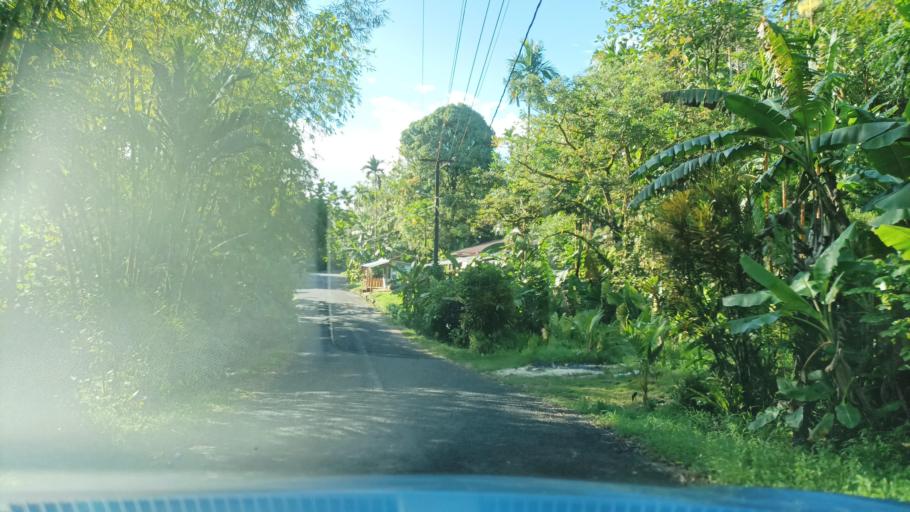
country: FM
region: Pohnpei
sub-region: Kolonia Municipality
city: Kolonia Town
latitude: 6.9561
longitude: 158.1868
